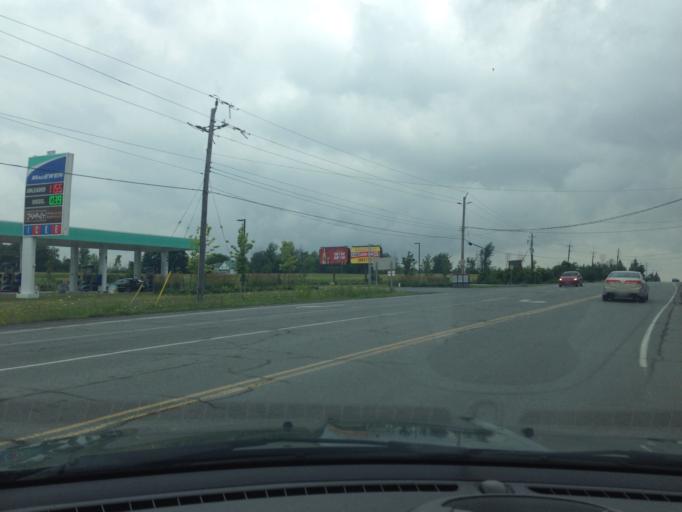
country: CA
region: Ontario
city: Ottawa
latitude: 45.2970
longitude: -75.5799
